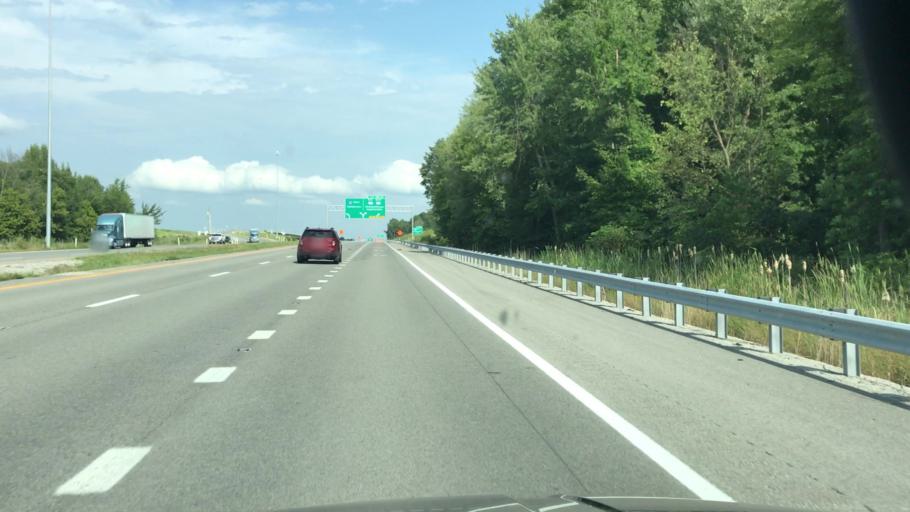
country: US
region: Kentucky
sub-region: Hopkins County
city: Nortonville
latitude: 37.2124
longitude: -87.4567
